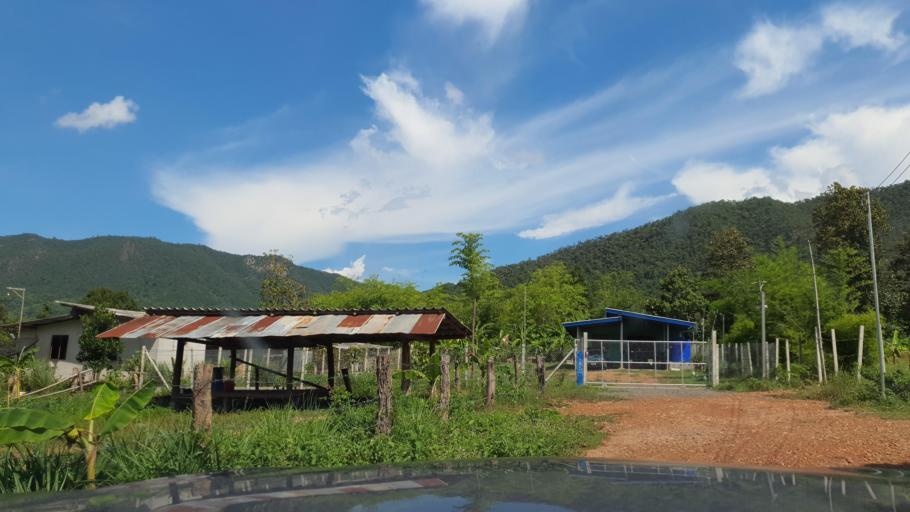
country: TH
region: Chiang Mai
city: Mae On
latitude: 18.7406
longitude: 99.2471
